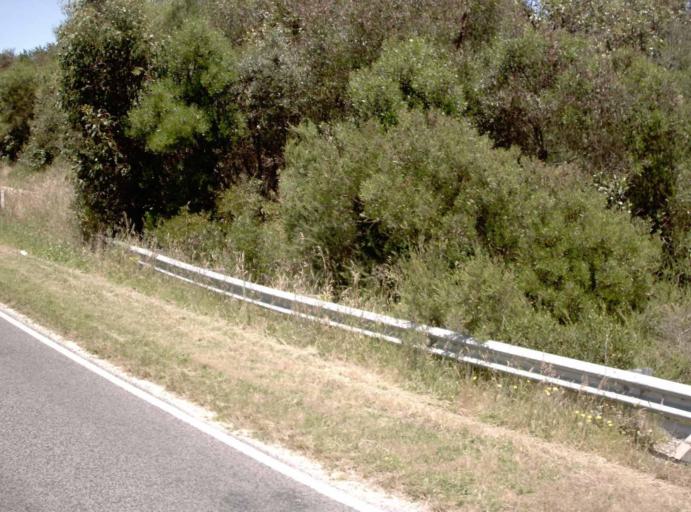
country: AU
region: Victoria
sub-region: Bass Coast
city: North Wonthaggi
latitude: -38.7704
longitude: 146.1588
